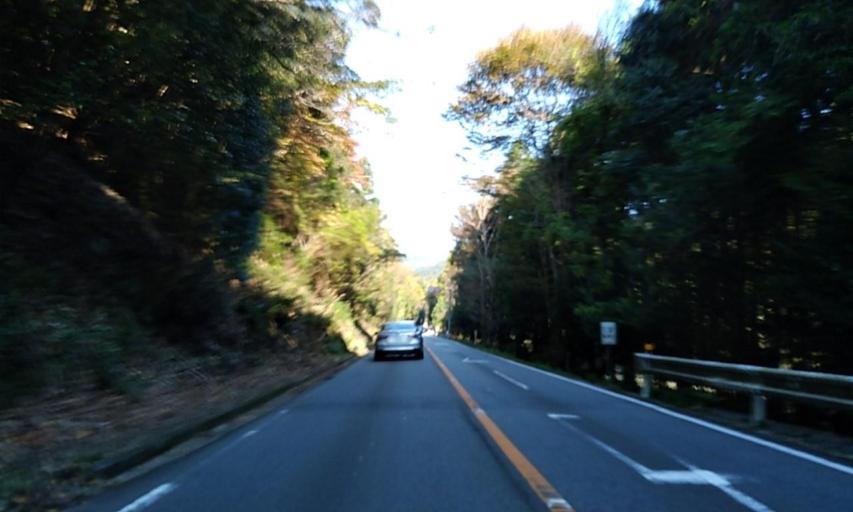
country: JP
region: Mie
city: Ise
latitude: 34.4464
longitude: 136.7504
